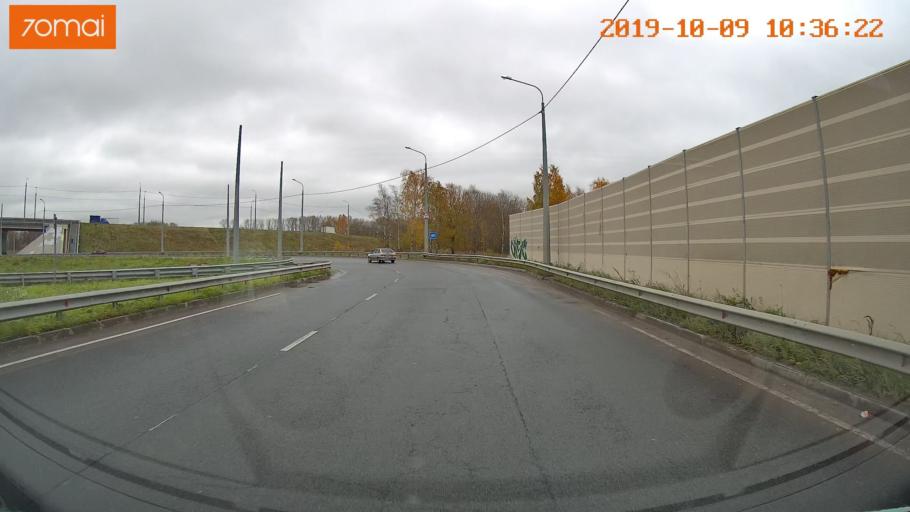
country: RU
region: Vologda
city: Vologda
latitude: 59.2327
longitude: 39.8655
